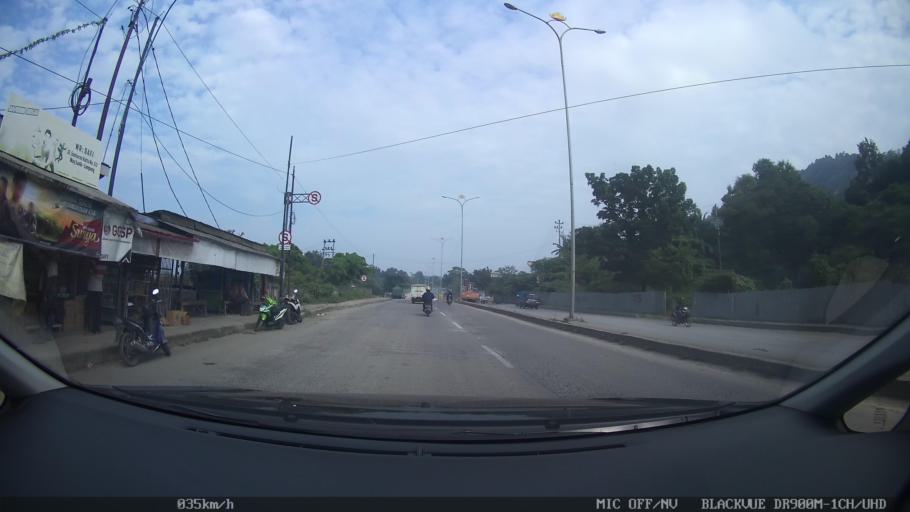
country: ID
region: Lampung
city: Panjang
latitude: -5.4423
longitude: 105.3099
